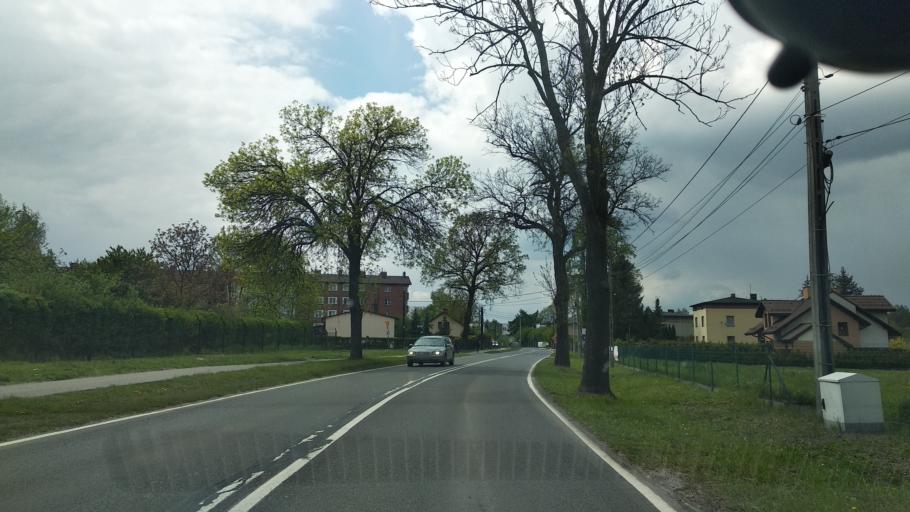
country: PL
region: Silesian Voivodeship
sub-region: Powiat mikolowski
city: Mikolow
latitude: 50.2296
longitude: 18.9394
